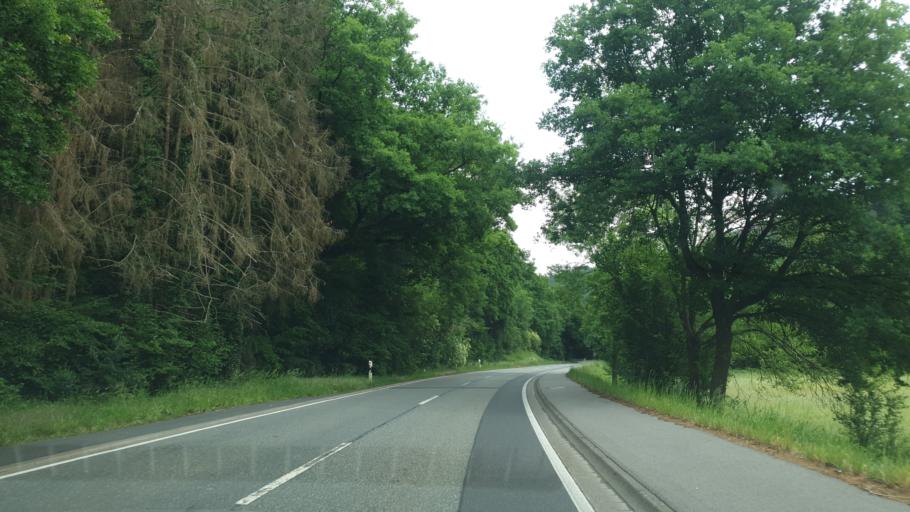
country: DE
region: Rheinland-Pfalz
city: Nassau
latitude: 50.3099
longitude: 7.8229
